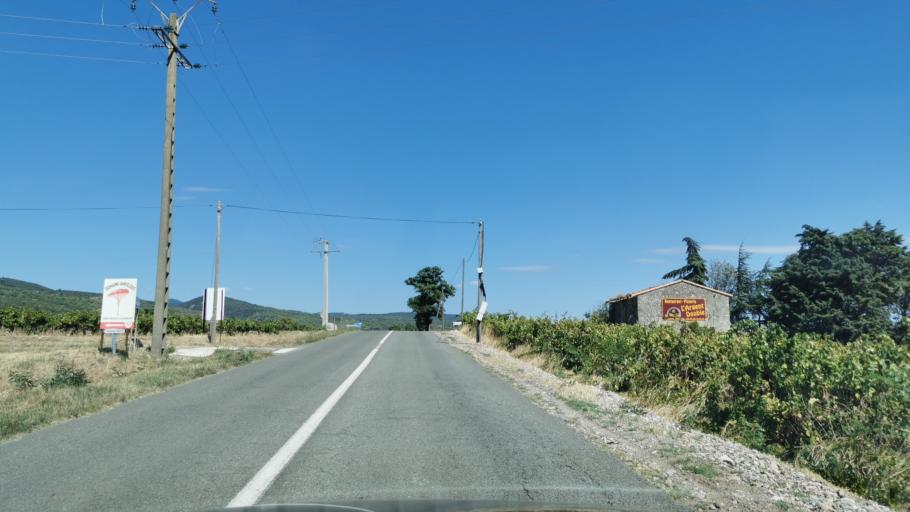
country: FR
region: Languedoc-Roussillon
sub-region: Departement de l'Aude
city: Caunes-Minervois
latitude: 43.3149
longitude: 2.5032
